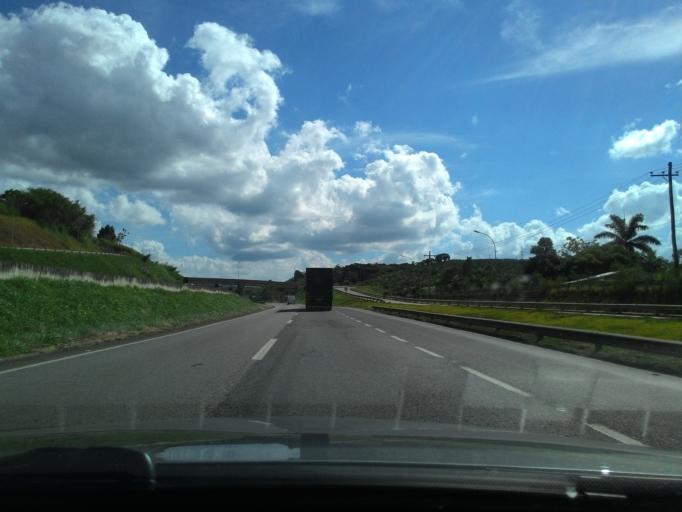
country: BR
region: Sao Paulo
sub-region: Cajati
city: Cajati
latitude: -24.7365
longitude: -48.1199
